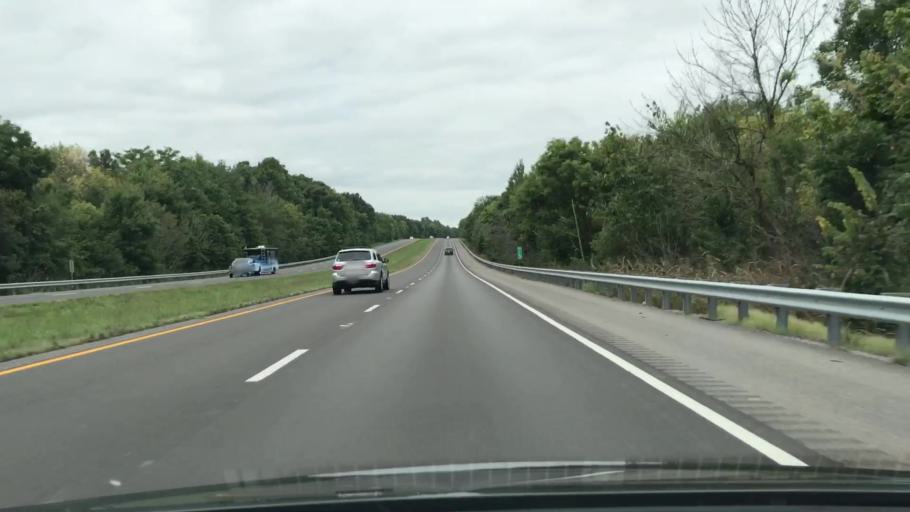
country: US
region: Kentucky
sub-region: Graves County
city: Mayfield
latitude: 36.6632
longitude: -88.7411
